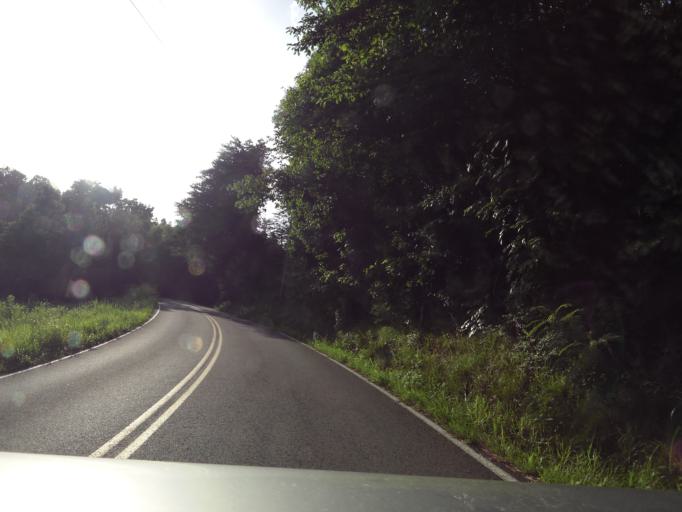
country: US
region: Tennessee
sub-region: Blount County
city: Wildwood
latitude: 35.8475
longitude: -83.8715
